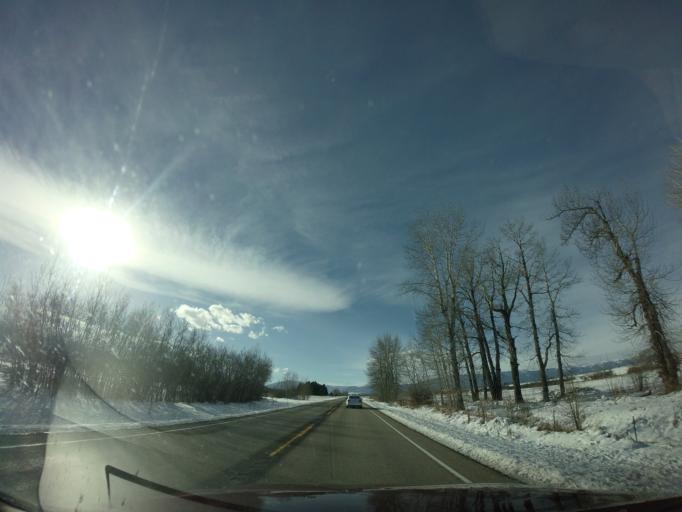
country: US
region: Montana
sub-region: Carbon County
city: Red Lodge
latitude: 45.2995
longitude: -109.2041
